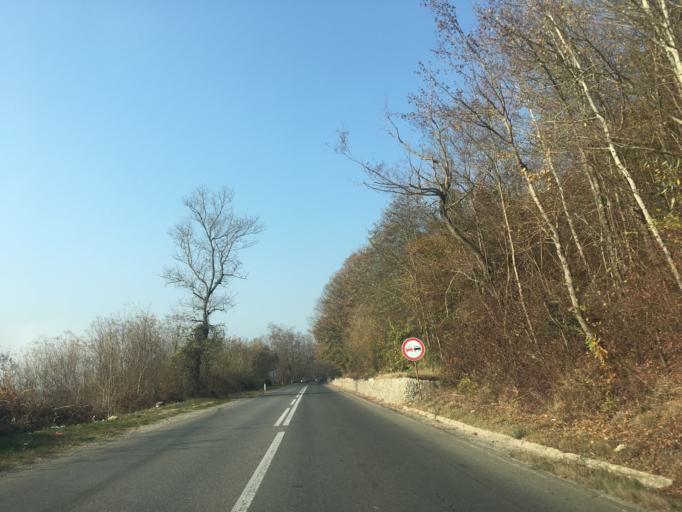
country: XK
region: Pec
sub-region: Komuna e Pejes
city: Kosuriq
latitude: 42.6384
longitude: 20.4323
